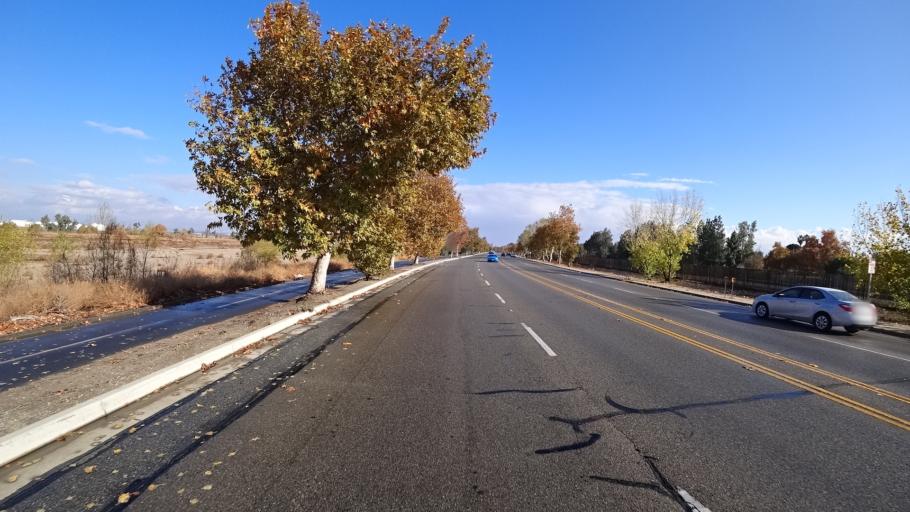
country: US
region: California
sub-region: Kern County
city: Greenacres
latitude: 35.3626
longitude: -119.0861
